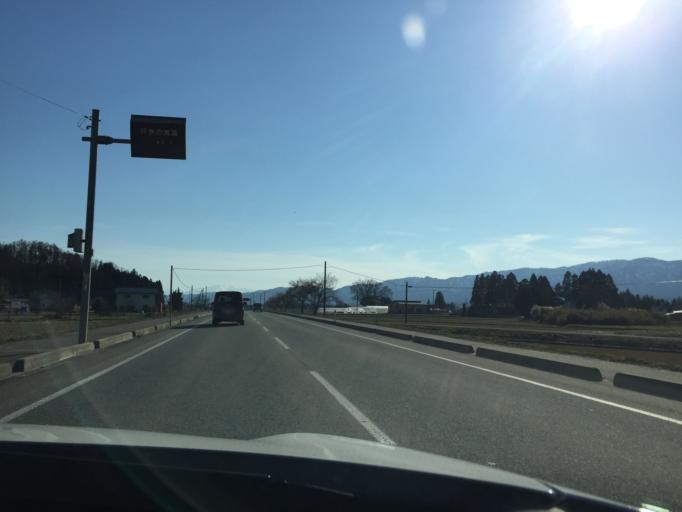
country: JP
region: Yamagata
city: Nagai
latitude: 38.1563
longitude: 140.0702
